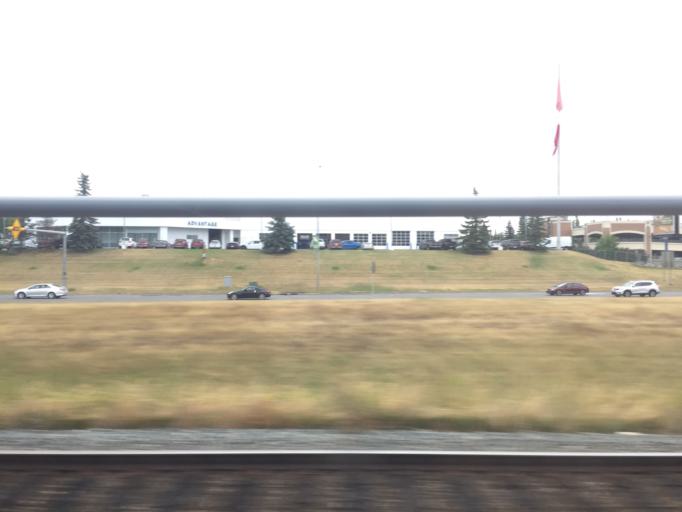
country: CA
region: Alberta
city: Calgary
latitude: 50.9373
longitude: -114.0697
